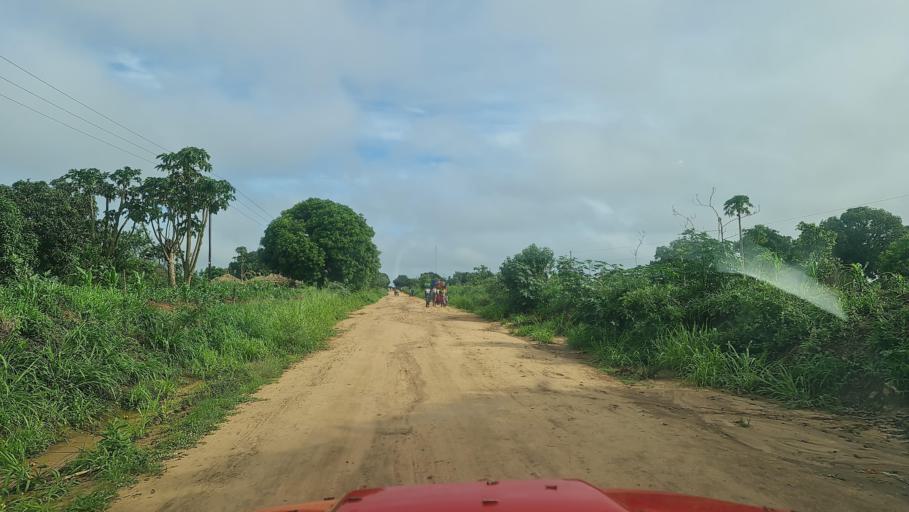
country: MW
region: Southern Region
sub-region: Nsanje District
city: Nsanje
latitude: -17.3058
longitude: 35.5932
